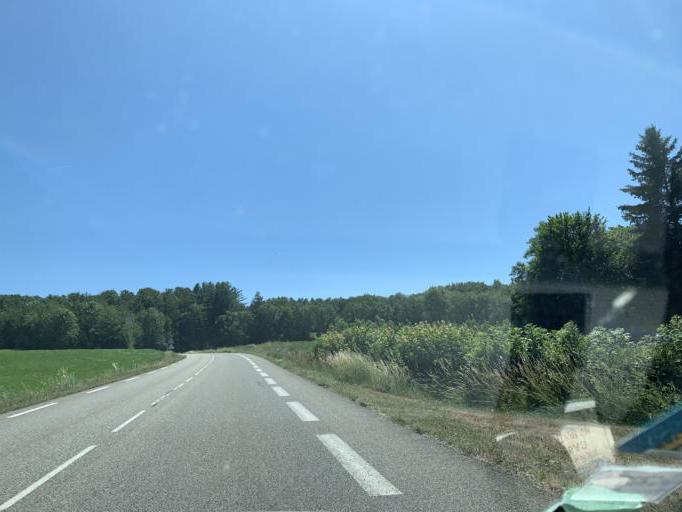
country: FR
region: Provence-Alpes-Cote d'Azur
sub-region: Departement des Hautes-Alpes
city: Saint-Bonnet-en-Champsaur
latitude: 44.6381
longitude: 6.1351
